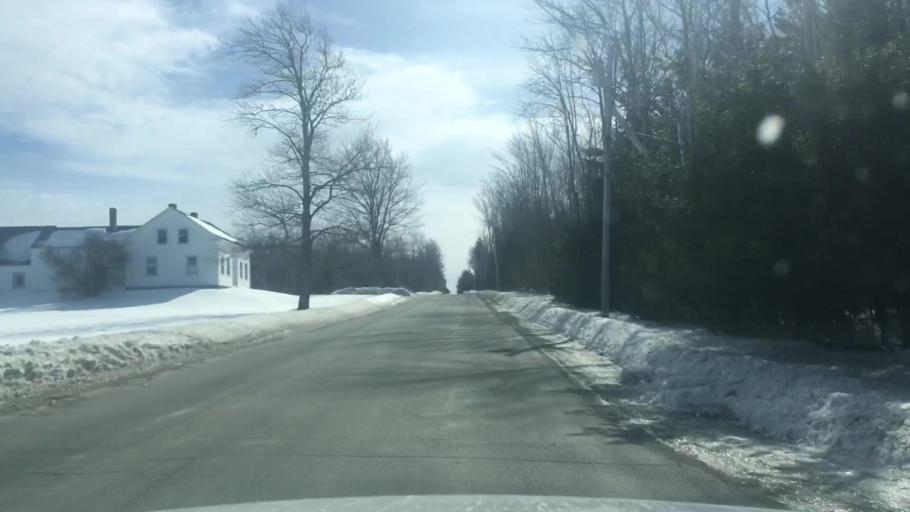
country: US
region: Maine
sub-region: Penobscot County
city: Holden
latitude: 44.7744
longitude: -68.6503
